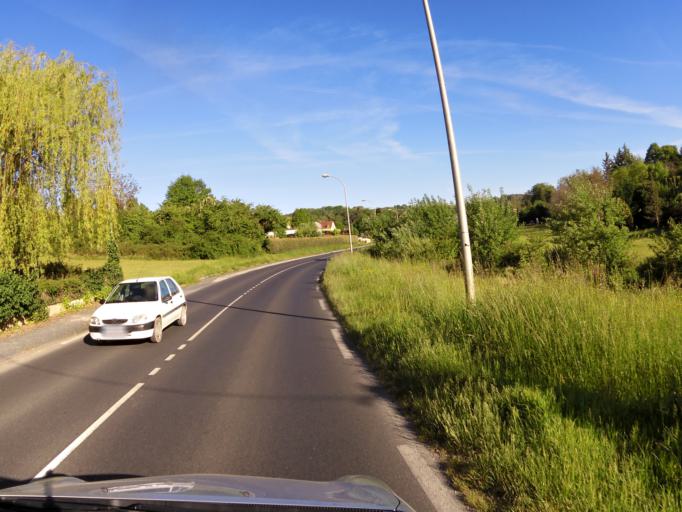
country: FR
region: Aquitaine
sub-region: Departement de la Dordogne
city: Sarlat-la-Caneda
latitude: 44.9042
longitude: 1.2091
